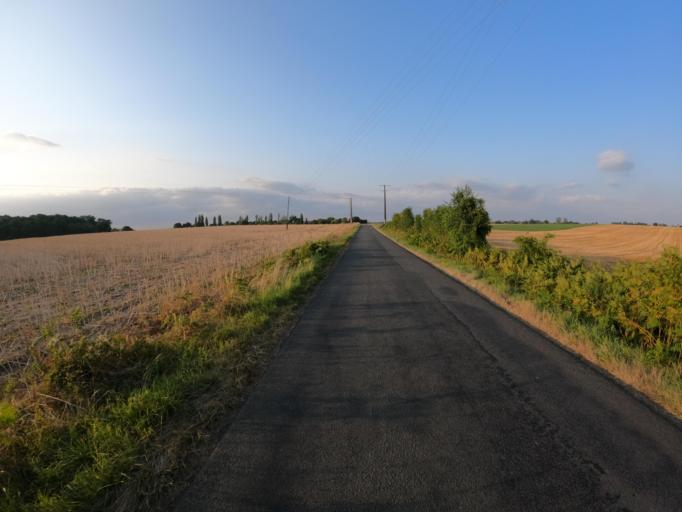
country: FR
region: Pays de la Loire
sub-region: Departement de la Sarthe
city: Parce-sur-Sarthe
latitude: 47.8863
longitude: -0.2202
